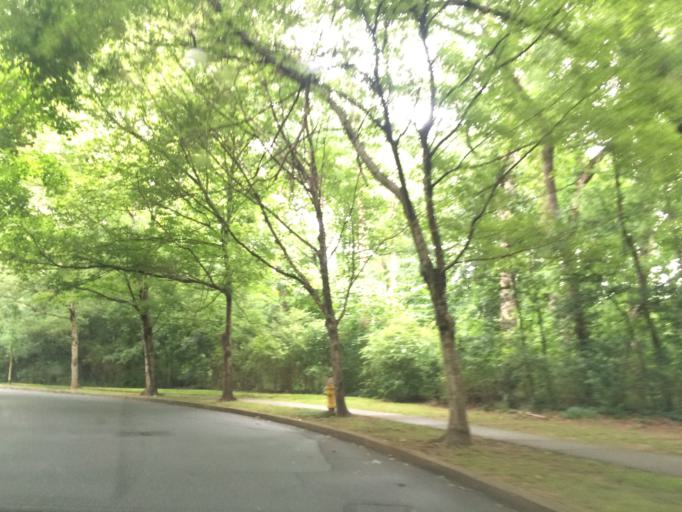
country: US
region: Georgia
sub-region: DeKalb County
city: Druid Hills
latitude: 33.7949
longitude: -84.3307
